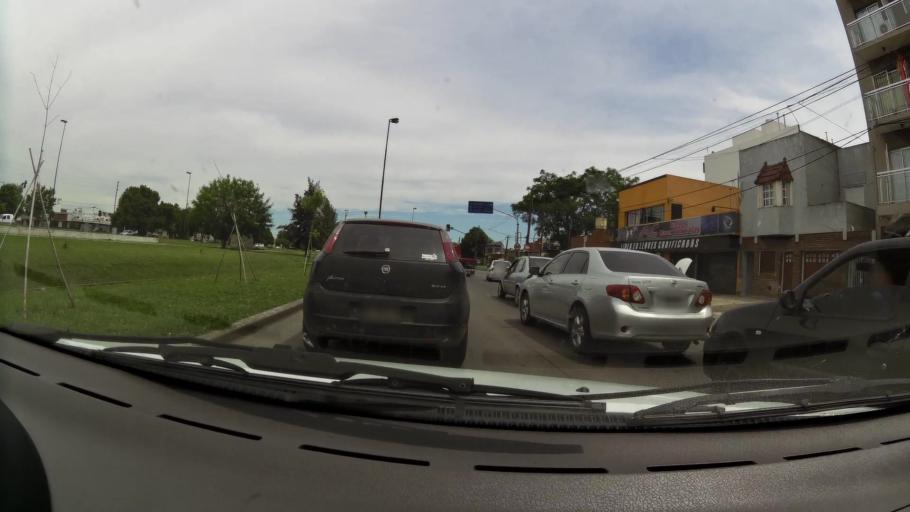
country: AR
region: Buenos Aires
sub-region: Partido de La Plata
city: La Plata
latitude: -34.9475
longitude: -57.9460
